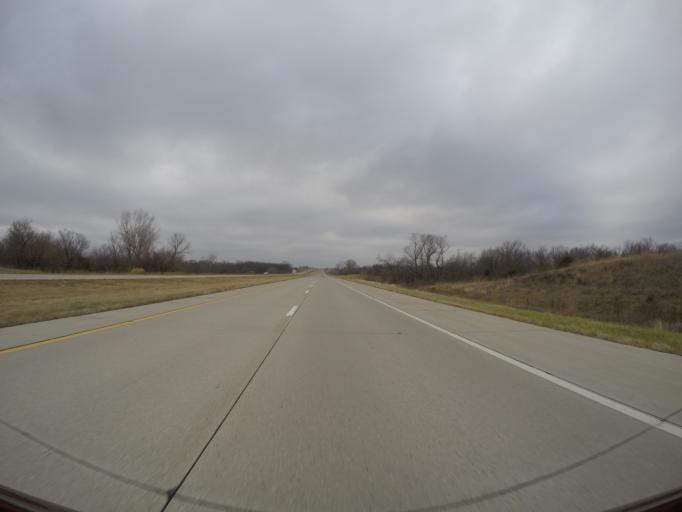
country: US
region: Kansas
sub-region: Dickinson County
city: Chapman
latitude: 38.9944
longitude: -96.9645
